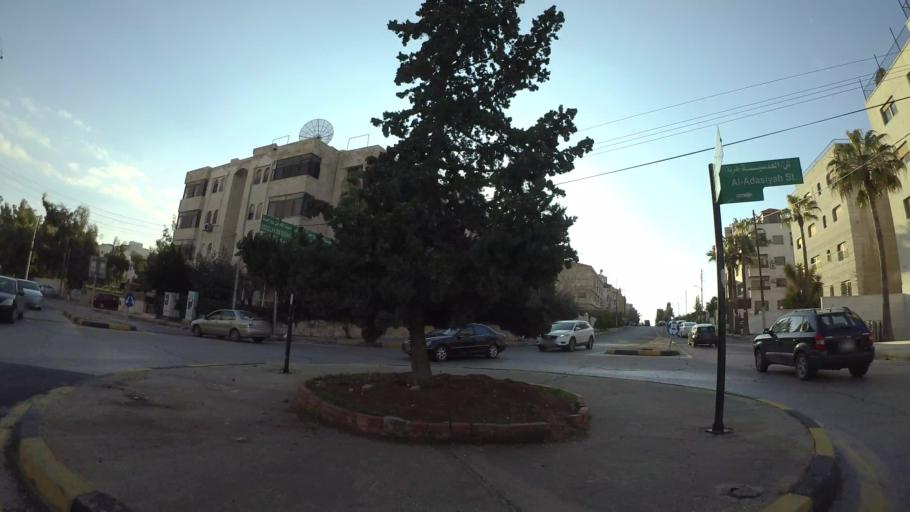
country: JO
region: Amman
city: Al Jubayhah
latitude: 31.9737
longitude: 35.8793
